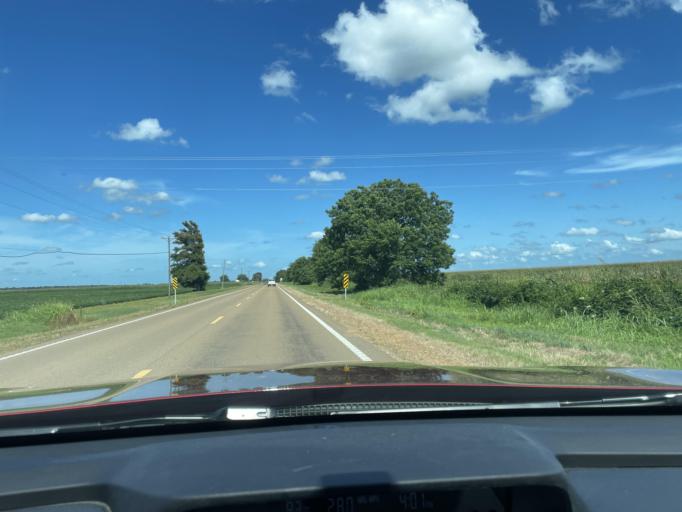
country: US
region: Mississippi
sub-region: Humphreys County
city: Belzoni
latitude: 33.1837
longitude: -90.5351
